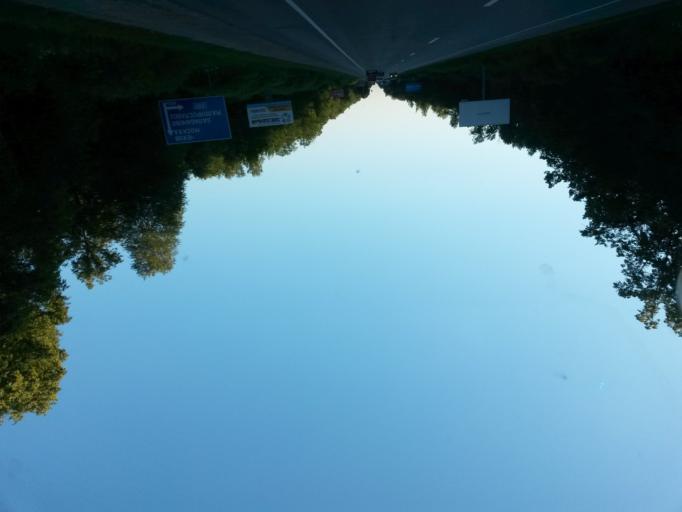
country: RU
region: Moskovskaya
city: Serpukhov
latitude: 54.9713
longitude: 37.4140
